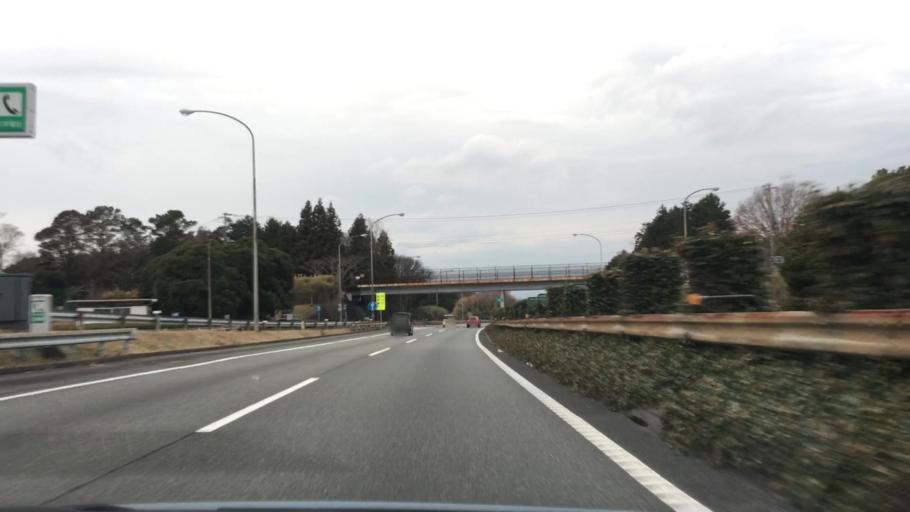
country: JP
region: Shizuoka
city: Numazu
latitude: 35.1429
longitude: 138.8360
